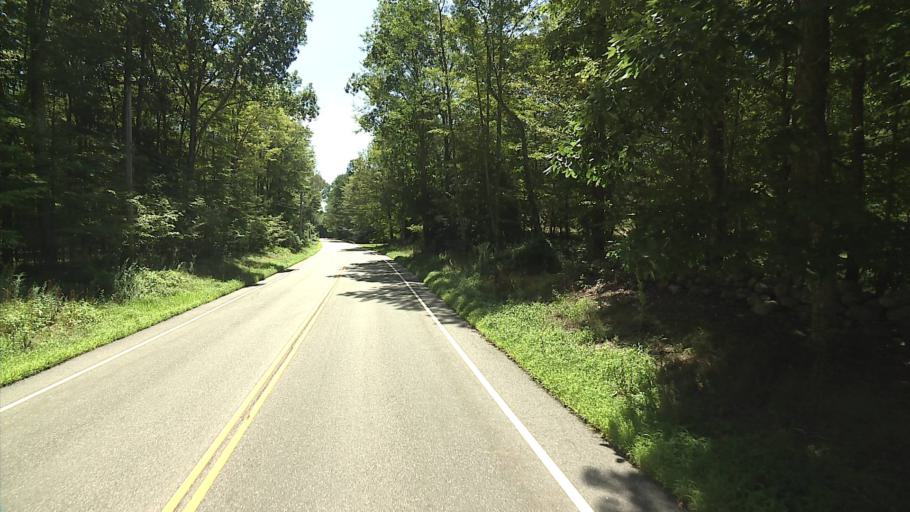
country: US
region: Connecticut
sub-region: Windham County
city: East Brooklyn
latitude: 41.8124
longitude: -72.0448
